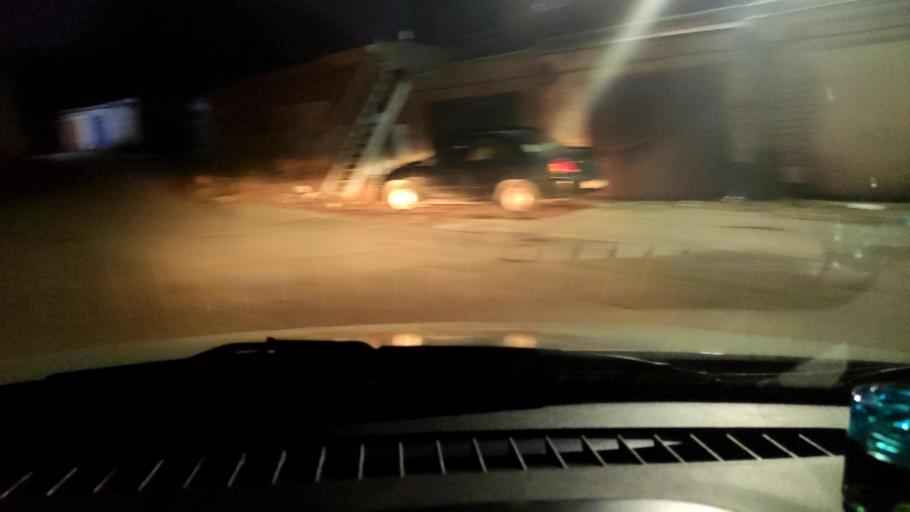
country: RU
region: Voronezj
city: Voronezh
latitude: 51.6363
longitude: 39.1331
